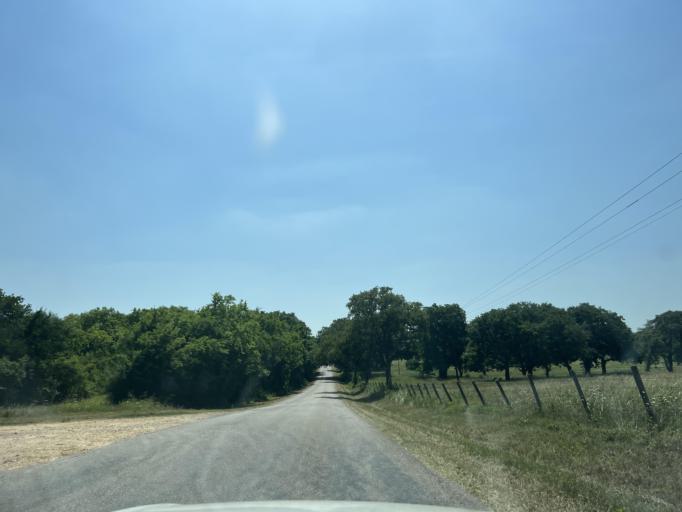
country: US
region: Texas
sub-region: Washington County
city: Brenham
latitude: 30.1602
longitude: -96.4434
